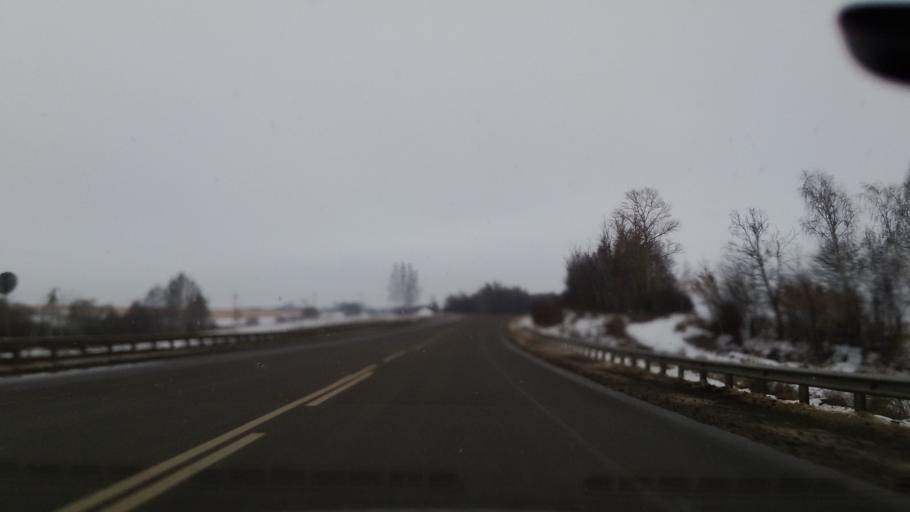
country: RU
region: Tula
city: Bolokhovo
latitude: 54.0375
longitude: 37.8738
